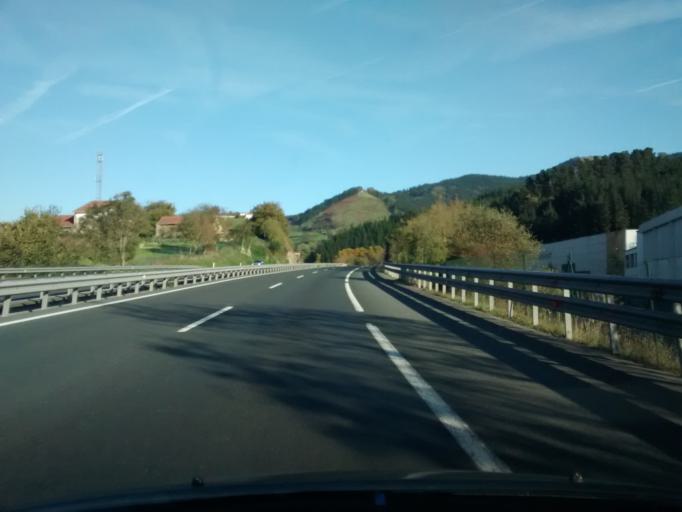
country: ES
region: Basque Country
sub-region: Bizkaia
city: Berriz
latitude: 43.1674
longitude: -2.5564
